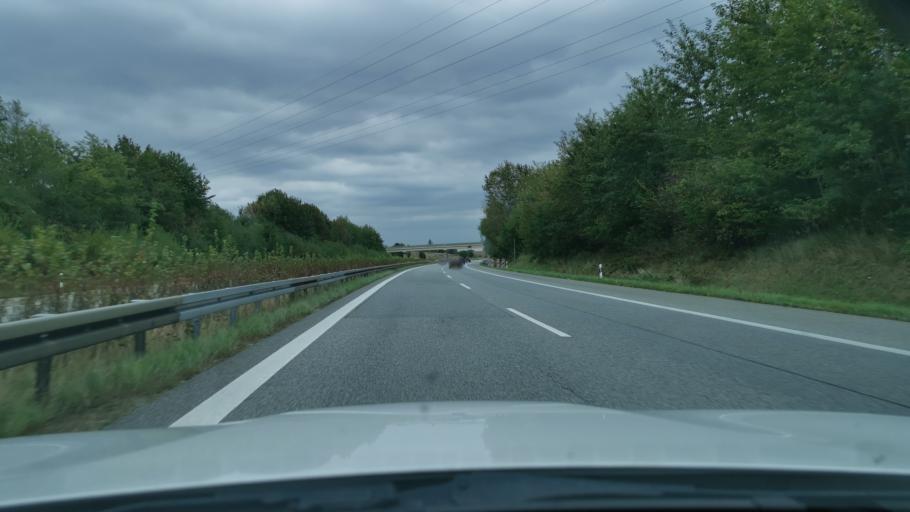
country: DE
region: Mecklenburg-Vorpommern
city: Lalendorf
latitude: 53.7238
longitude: 12.3563
